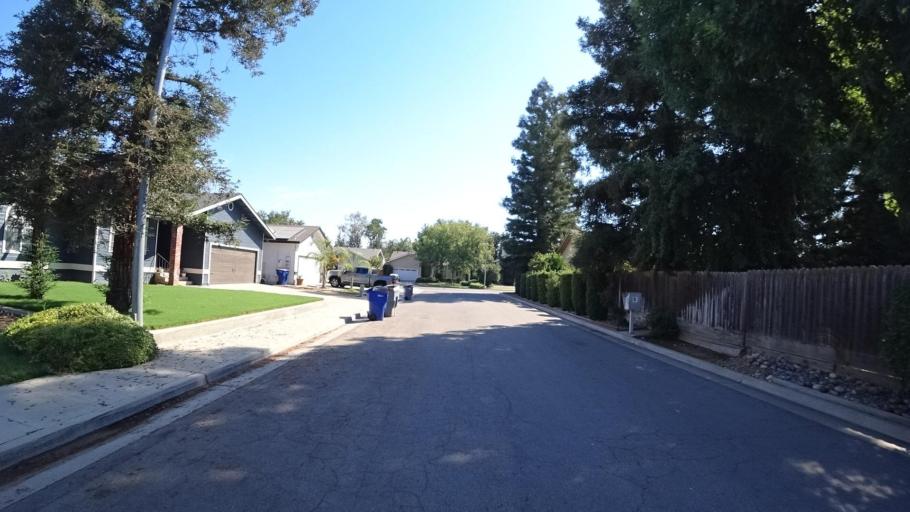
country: US
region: California
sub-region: Fresno County
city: Sunnyside
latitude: 36.7446
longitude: -119.6806
